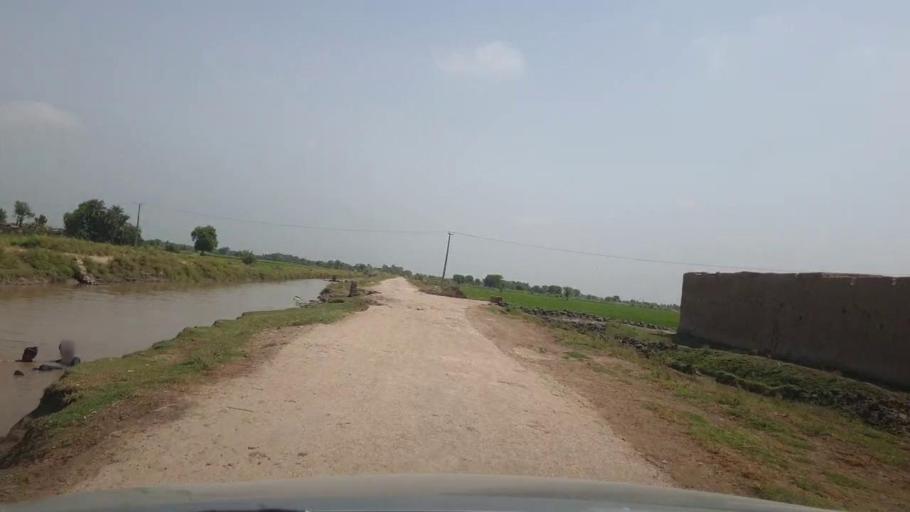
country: PK
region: Sindh
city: Ratodero
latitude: 27.9272
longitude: 68.3599
